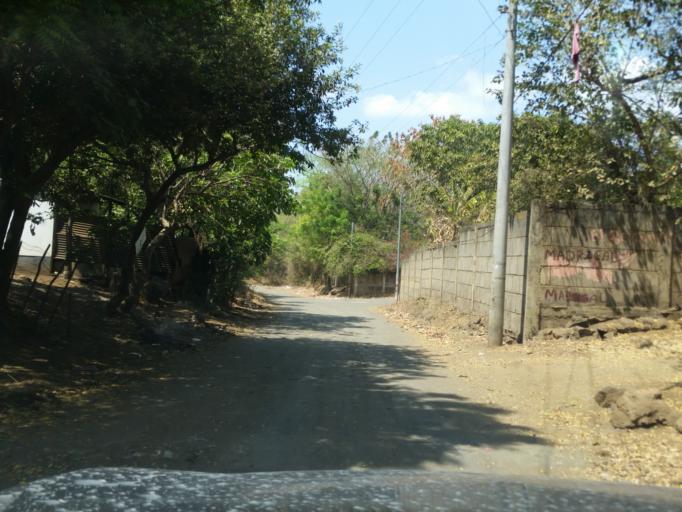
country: NI
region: Masaya
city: Ticuantepe
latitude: 12.0822
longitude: -86.2114
